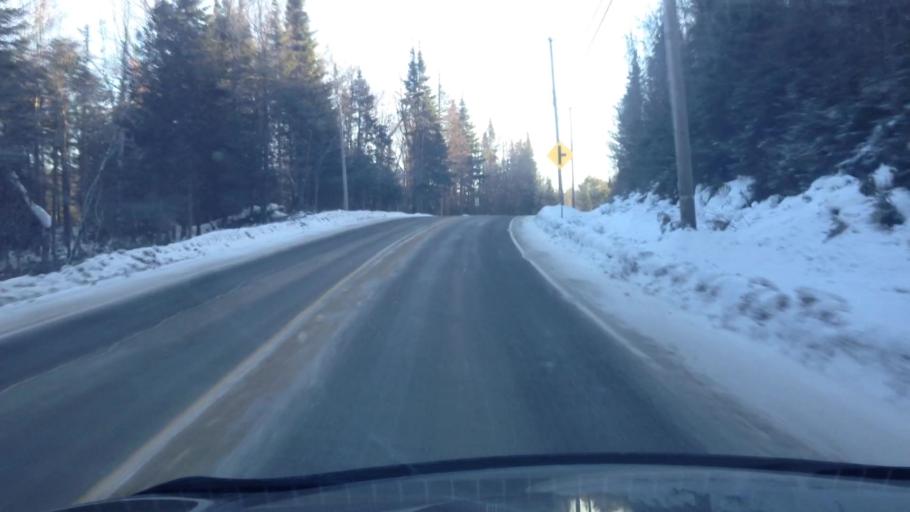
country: CA
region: Quebec
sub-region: Laurentides
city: Sainte-Agathe-des-Monts
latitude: 45.9107
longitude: -74.3469
